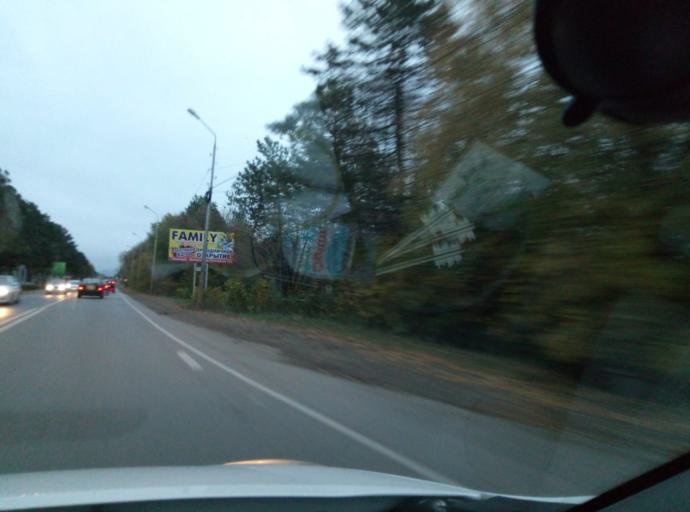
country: RU
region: Stavropol'skiy
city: Yessentukskaya
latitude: 44.0545
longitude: 42.9144
